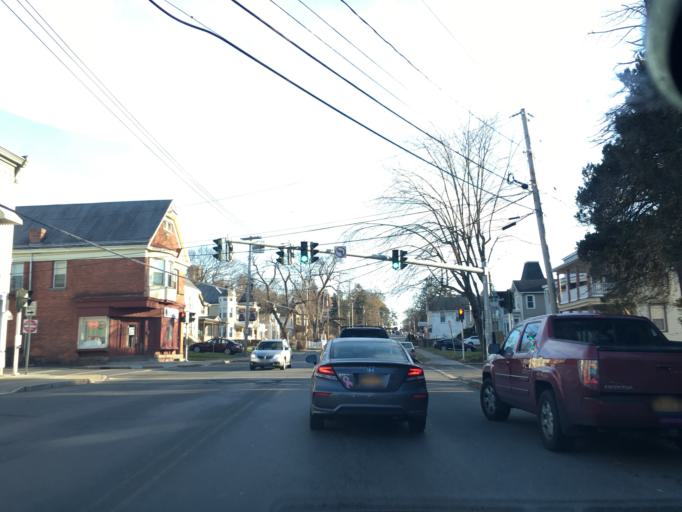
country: US
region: New York
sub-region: Rensselaer County
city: Troy
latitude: 42.7149
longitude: -73.6679
